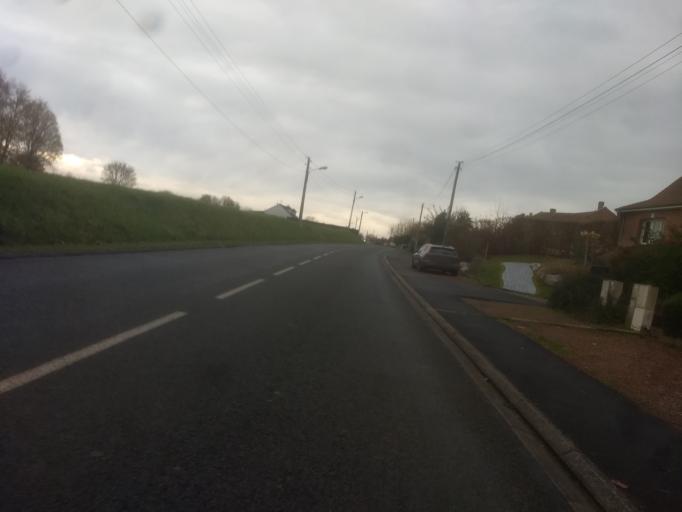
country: FR
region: Nord-Pas-de-Calais
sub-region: Departement du Pas-de-Calais
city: Riviere
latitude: 50.2378
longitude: 2.7063
